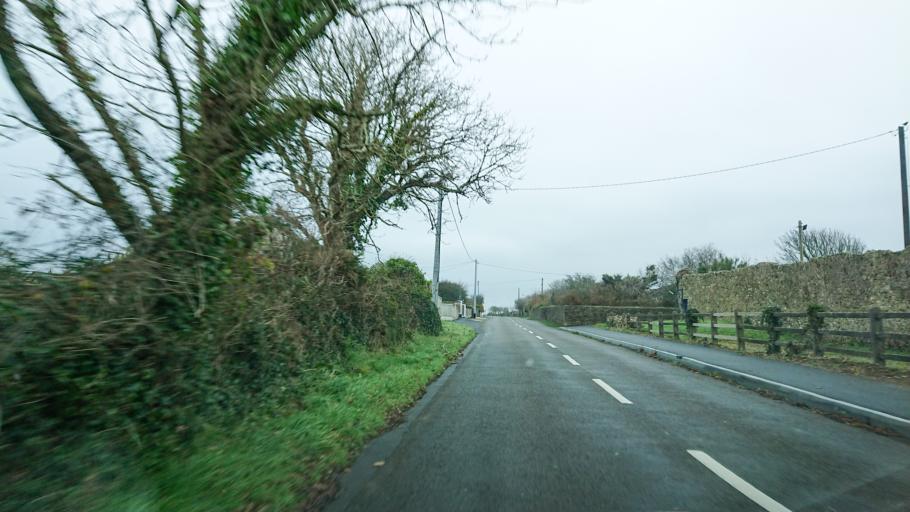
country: IE
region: Munster
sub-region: Waterford
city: Tra Mhor
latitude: 52.1508
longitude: -7.1700
